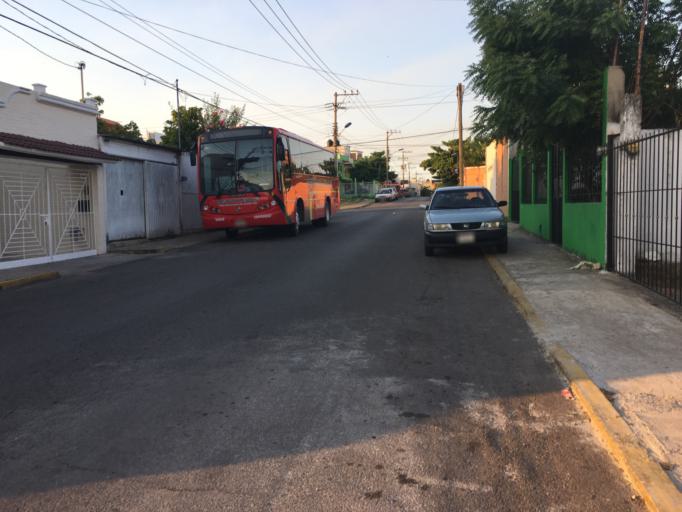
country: MX
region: Tabasco
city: Villahermosa
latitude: 17.9701
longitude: -92.9553
